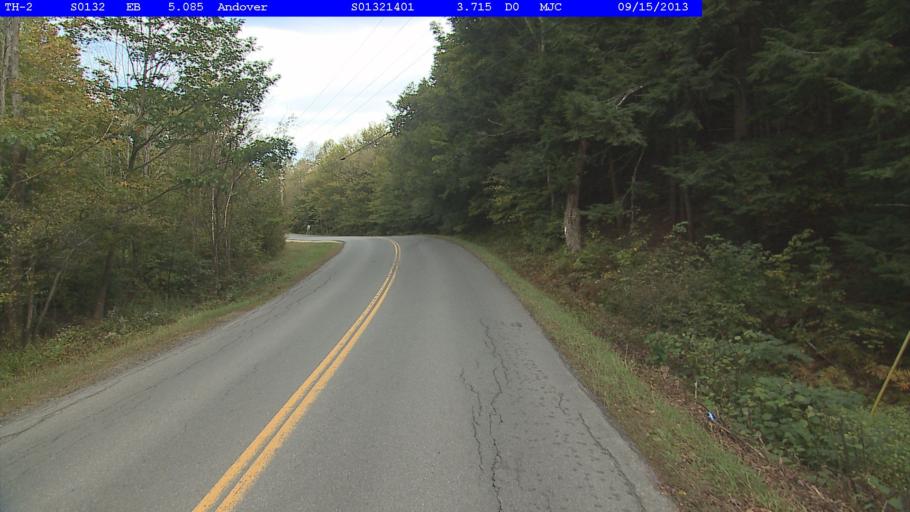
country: US
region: Vermont
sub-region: Windsor County
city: Chester
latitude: 43.2776
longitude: -72.7029
